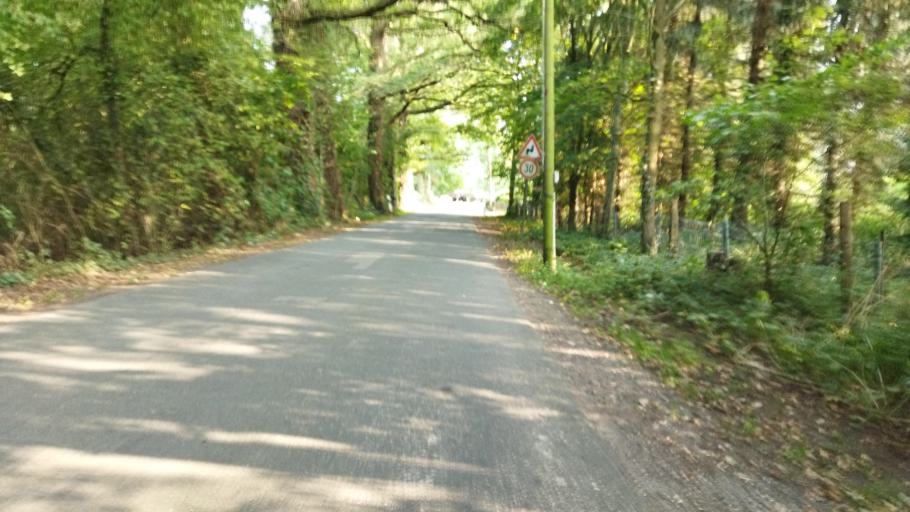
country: DE
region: Lower Saxony
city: Georgsmarienhutte
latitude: 52.2333
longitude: 8.0122
